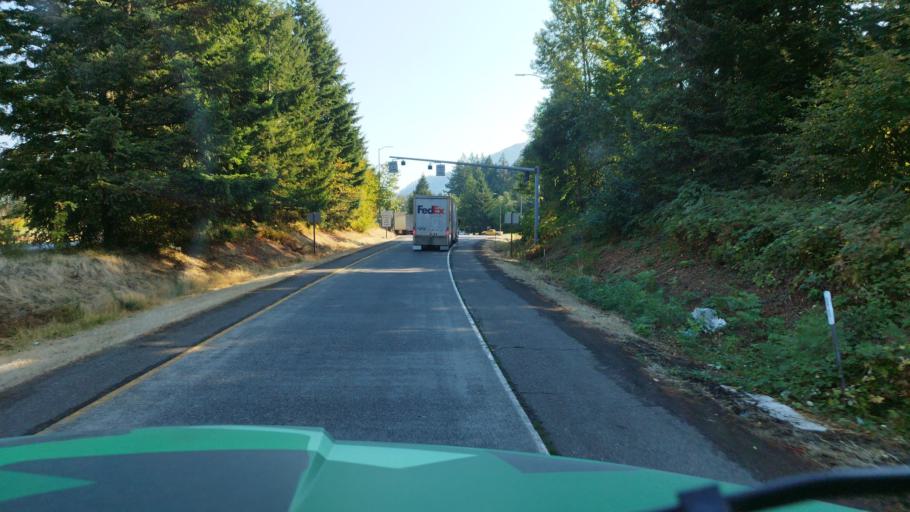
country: US
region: Oregon
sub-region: Hood River County
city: Cascade Locks
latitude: 45.6704
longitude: -121.8807
